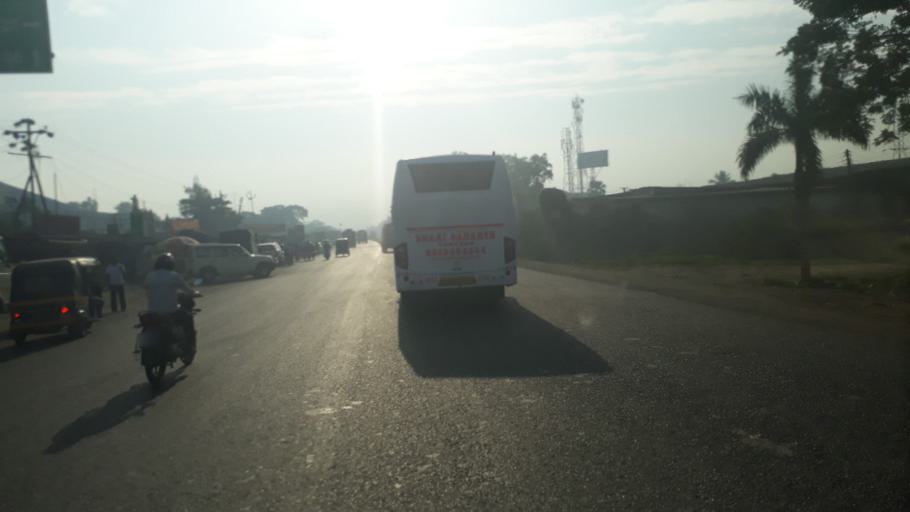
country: IN
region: Maharashtra
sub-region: Raigarh
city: Kalundri
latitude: 18.9700
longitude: 73.1328
